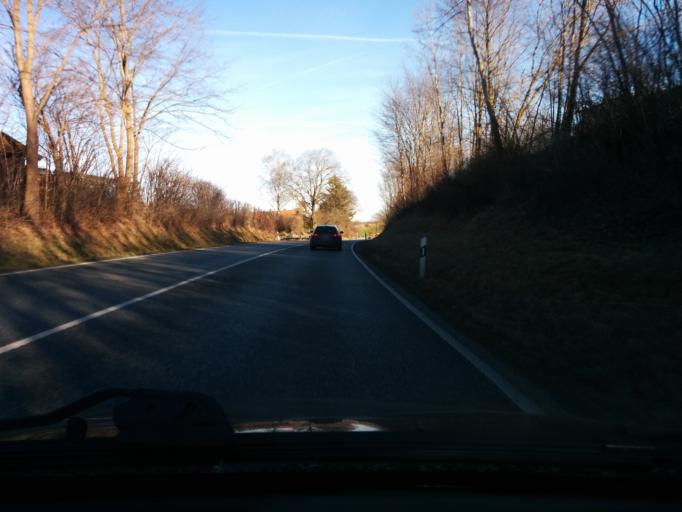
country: DE
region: Bavaria
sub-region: Upper Bavaria
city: Feldafing
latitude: 47.9393
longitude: 11.2561
